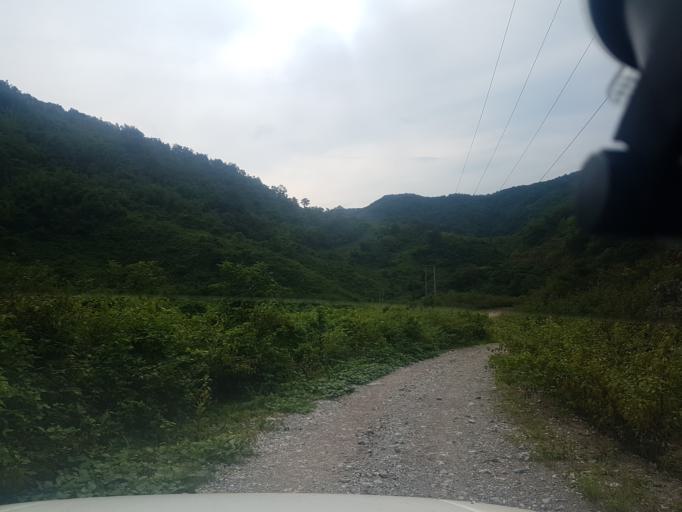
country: LA
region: Xiangkhoang
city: Phonsavan
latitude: 19.6901
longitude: 103.0815
